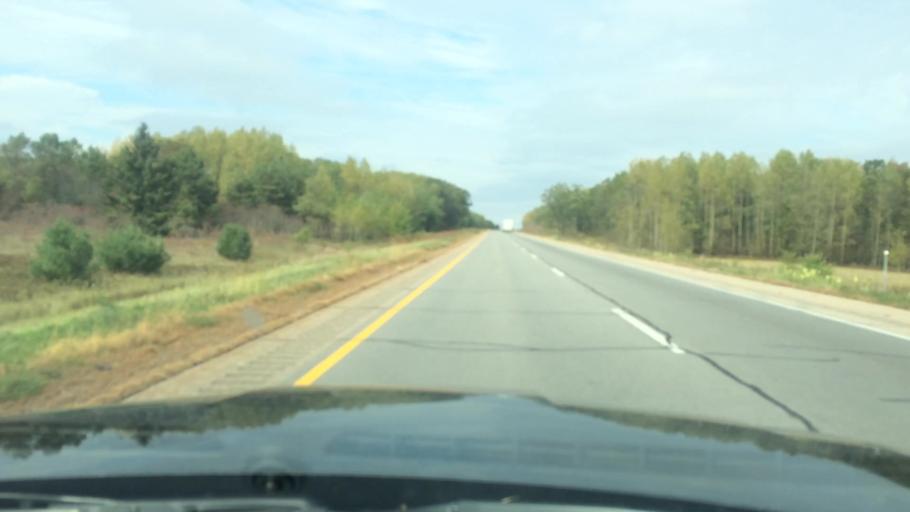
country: US
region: Wisconsin
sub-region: Marathon County
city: Mosinee
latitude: 44.6980
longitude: -89.6472
